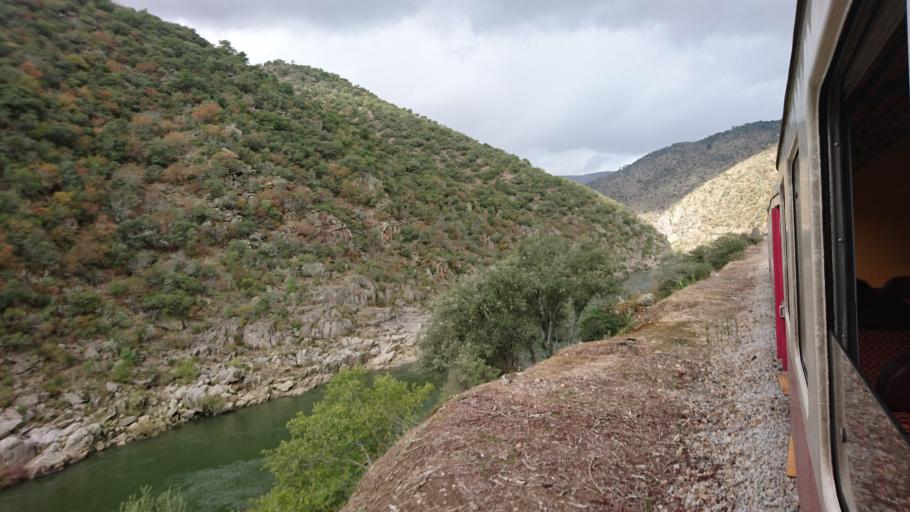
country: PT
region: Viseu
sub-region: Sao Joao da Pesqueira
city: Sao Joao da Pesqueira
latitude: 41.1874
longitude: -7.3864
